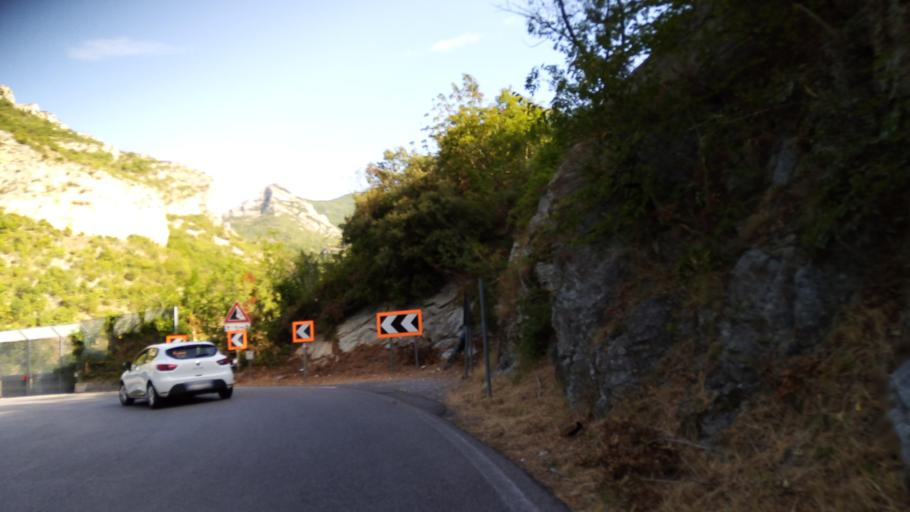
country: IT
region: Liguria
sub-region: Provincia di Savona
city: Balestrino
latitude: 44.1397
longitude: 8.1834
